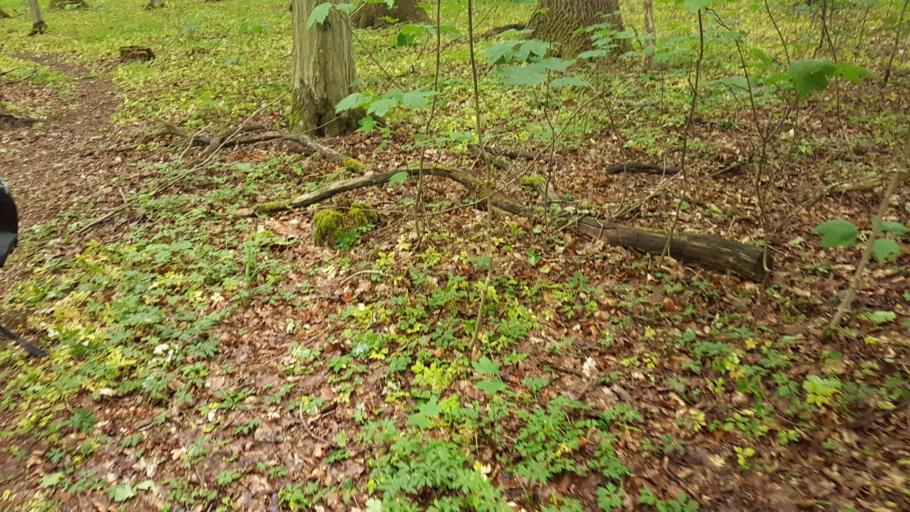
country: DE
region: Lower Saxony
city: Reppenstedt
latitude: 53.2226
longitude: 10.3565
